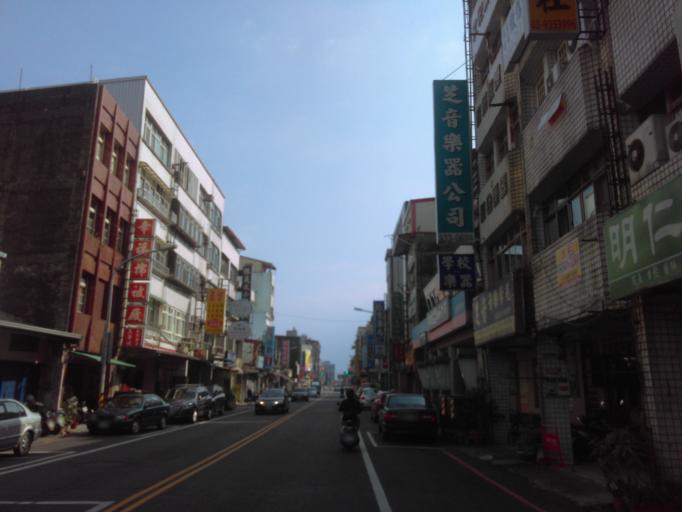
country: TW
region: Taiwan
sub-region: Yilan
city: Yilan
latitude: 24.7511
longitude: 121.7534
